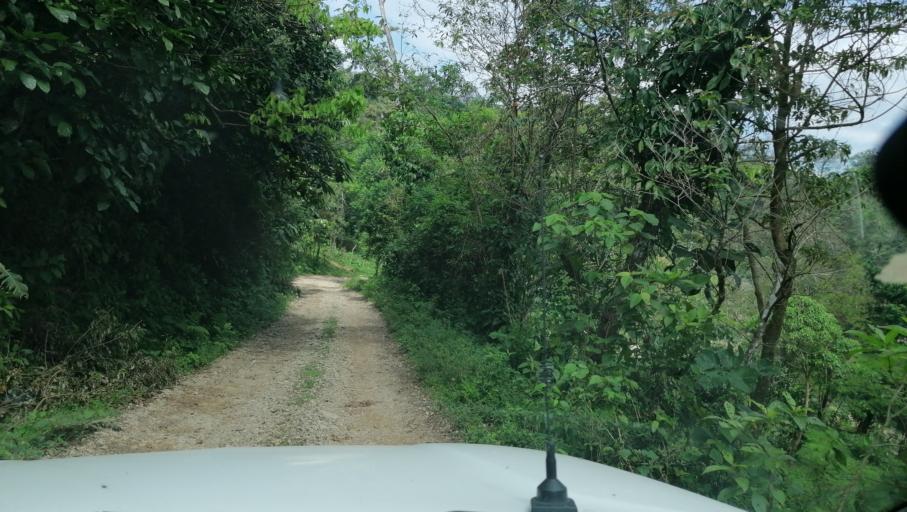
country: MX
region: Chiapas
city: Ixtacomitan
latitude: 17.3574
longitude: -93.1192
